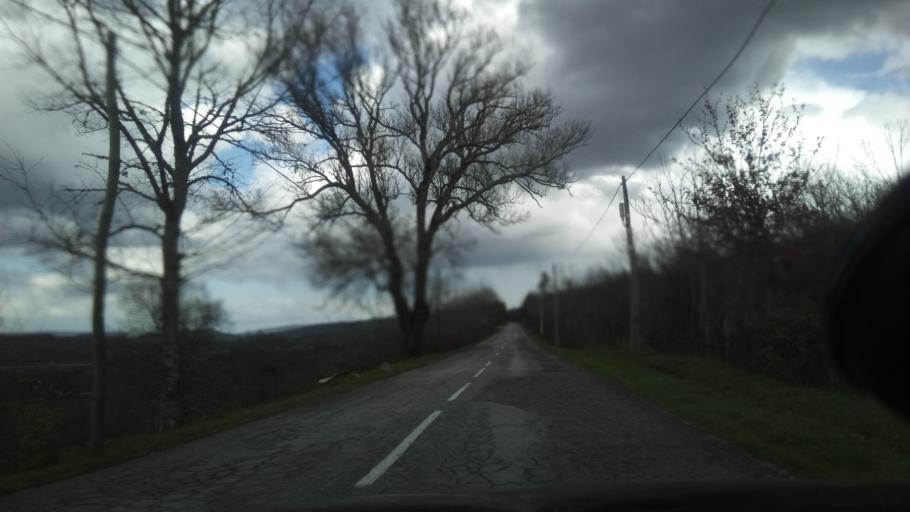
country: PT
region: Guarda
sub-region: Celorico da Beira
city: Celorico da Beira
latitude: 40.6278
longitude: -7.4543
